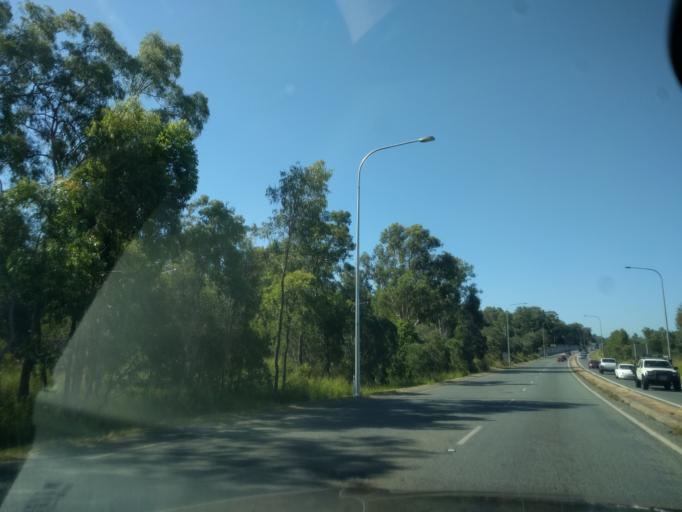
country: AU
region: Queensland
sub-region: Logan
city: Park Ridge South
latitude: -27.7235
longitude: 153.0306
